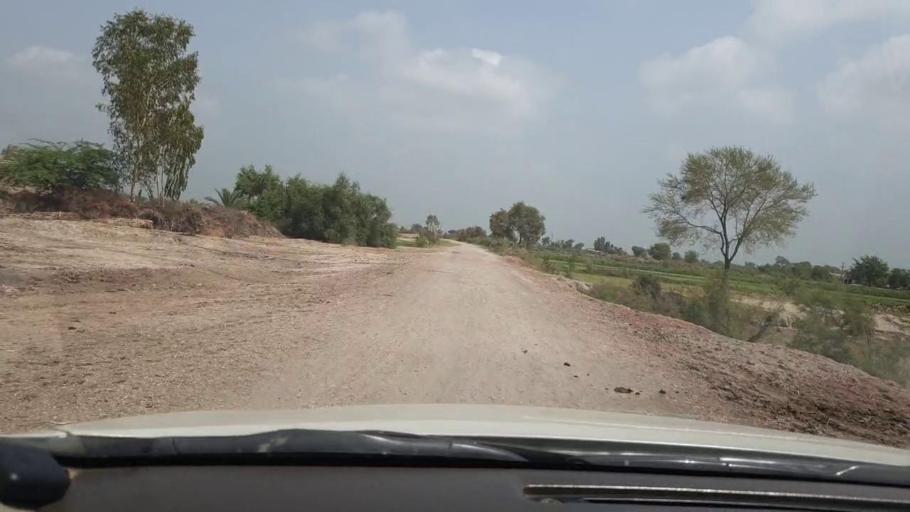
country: PK
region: Sindh
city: Garhi Yasin
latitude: 28.0158
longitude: 68.5286
